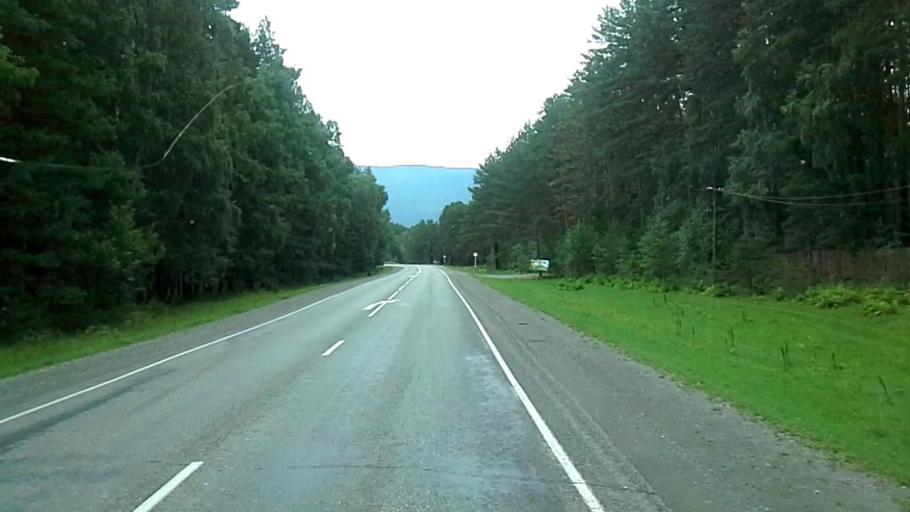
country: RU
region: Altay
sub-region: Mayminskiy Rayon
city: Manzherok
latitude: 51.8329
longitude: 85.7517
